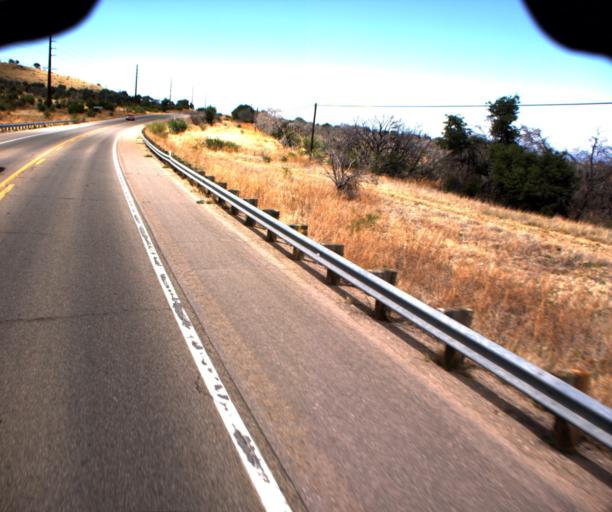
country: US
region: Arizona
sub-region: Cochise County
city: Sierra Vista Southeast
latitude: 31.4002
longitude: -110.2403
